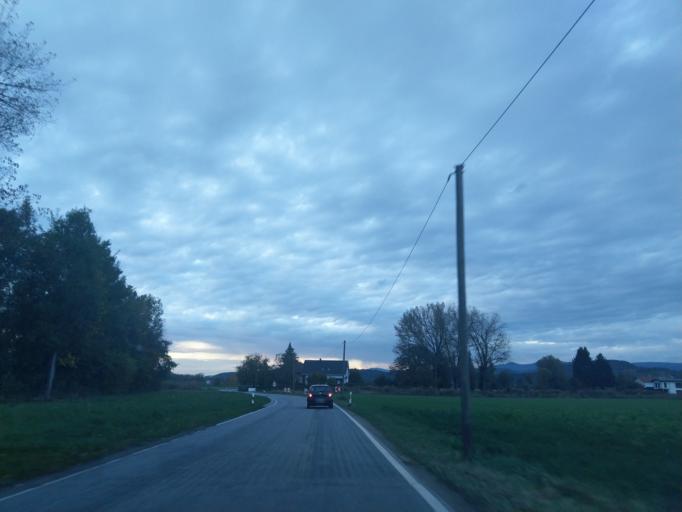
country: DE
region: Bavaria
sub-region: Lower Bavaria
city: Niederalteich
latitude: 48.7694
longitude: 13.0188
